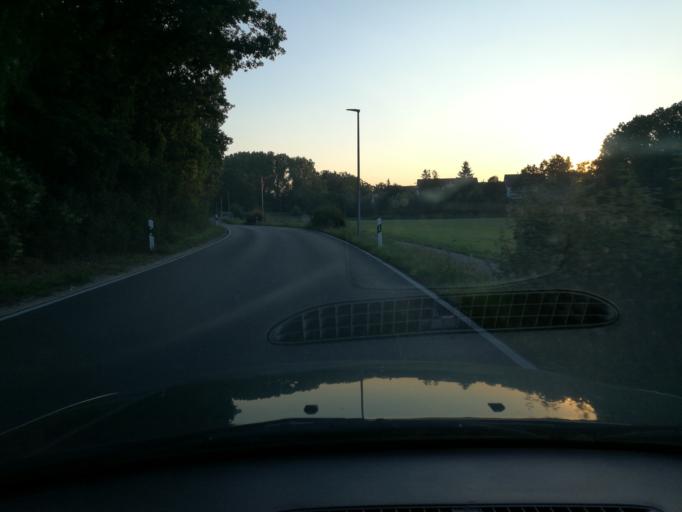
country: DE
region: Bavaria
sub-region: Regierungsbezirk Mittelfranken
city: Furth
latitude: 49.4961
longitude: 10.9677
